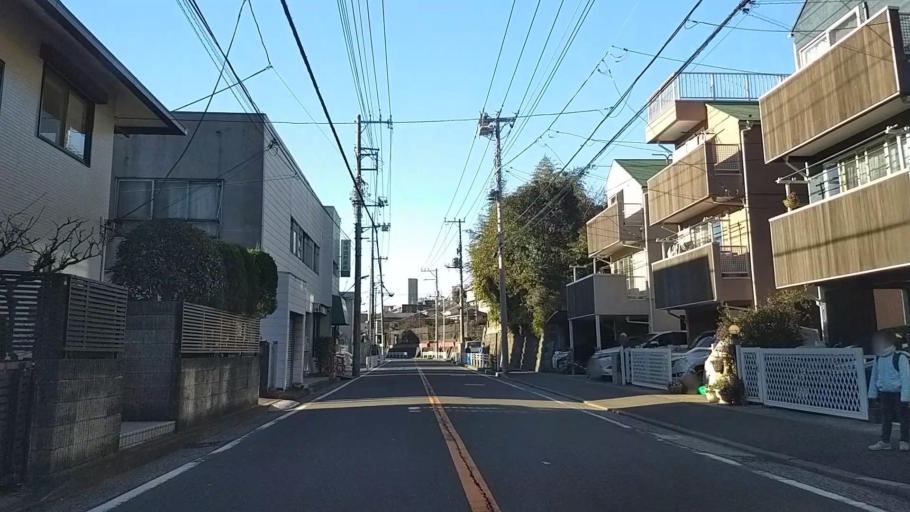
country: JP
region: Kanagawa
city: Yokohama
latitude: 35.4949
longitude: 139.6645
